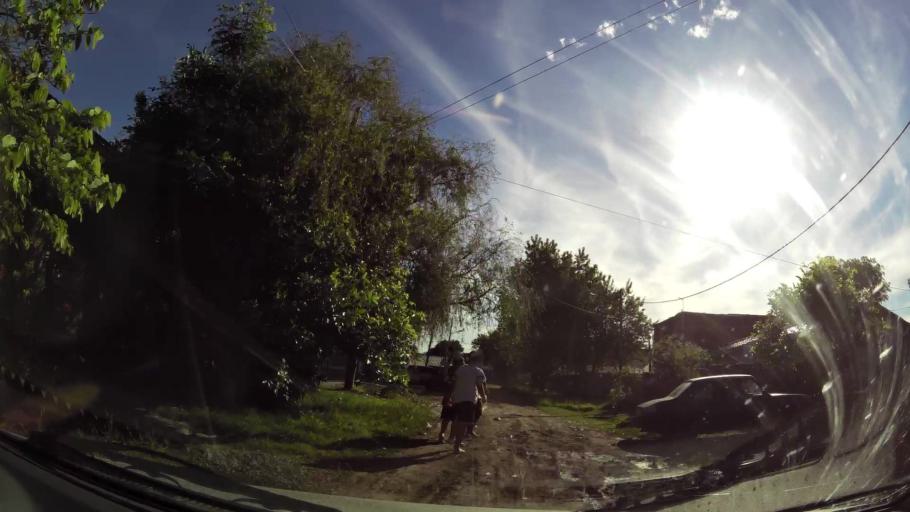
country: AR
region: Buenos Aires
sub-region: Partido de Almirante Brown
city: Adrogue
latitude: -34.8245
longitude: -58.3574
